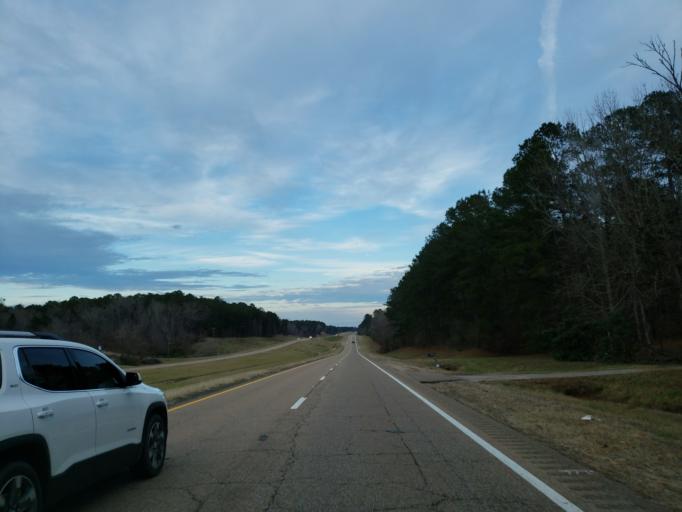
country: US
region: Mississippi
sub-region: Lauderdale County
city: Marion
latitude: 32.4761
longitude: -88.6034
